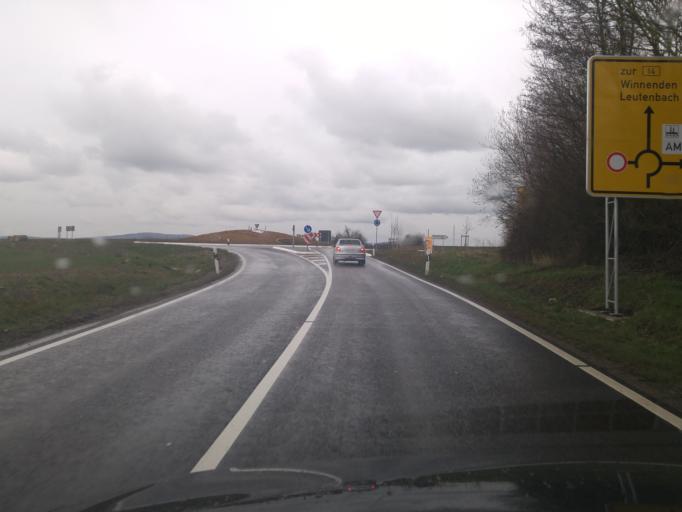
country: DE
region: Baden-Wuerttemberg
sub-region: Regierungsbezirk Stuttgart
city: Affalterbach
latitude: 48.9172
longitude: 9.3325
